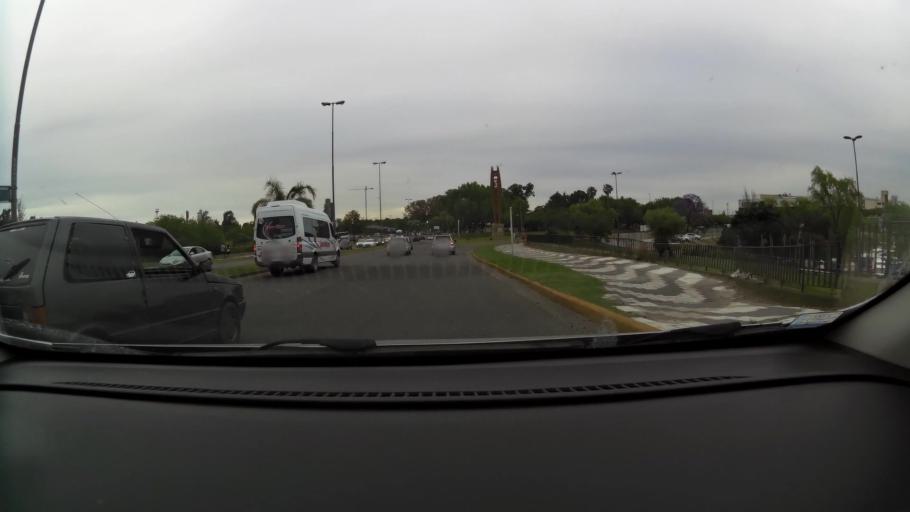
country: AR
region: Santa Fe
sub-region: Departamento de Rosario
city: Rosario
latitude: -32.9069
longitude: -60.6786
